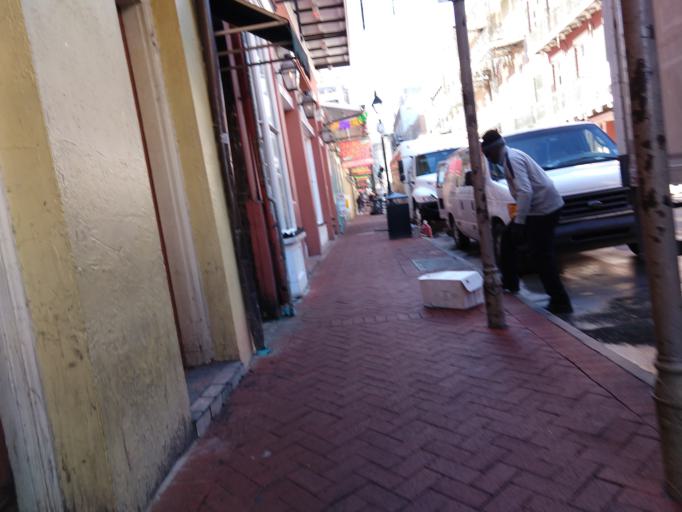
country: US
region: Louisiana
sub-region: Orleans Parish
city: New Orleans
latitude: 29.9553
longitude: -90.0685
